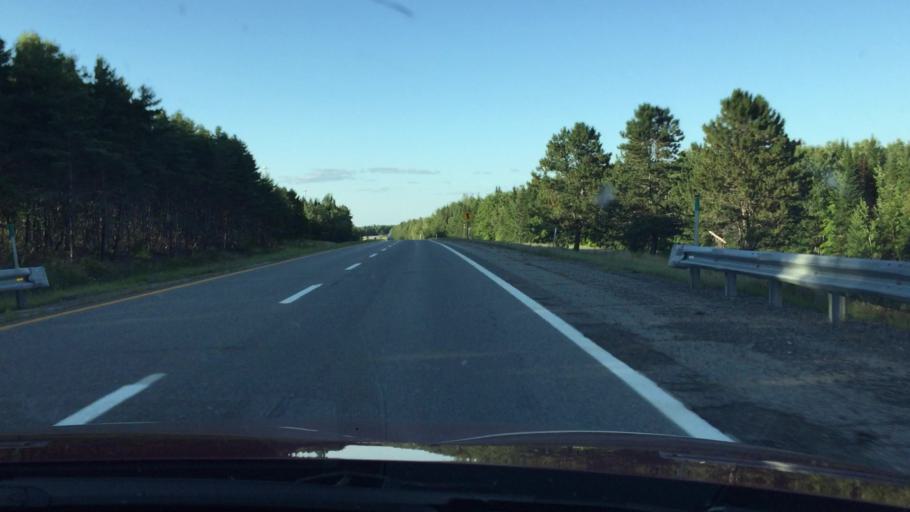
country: US
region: Maine
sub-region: Penobscot County
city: Patten
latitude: 45.8731
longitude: -68.4122
